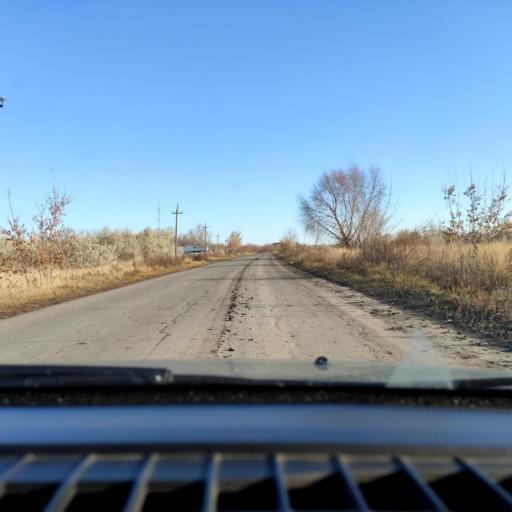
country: RU
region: Samara
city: Tol'yatti
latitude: 53.6374
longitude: 49.3104
